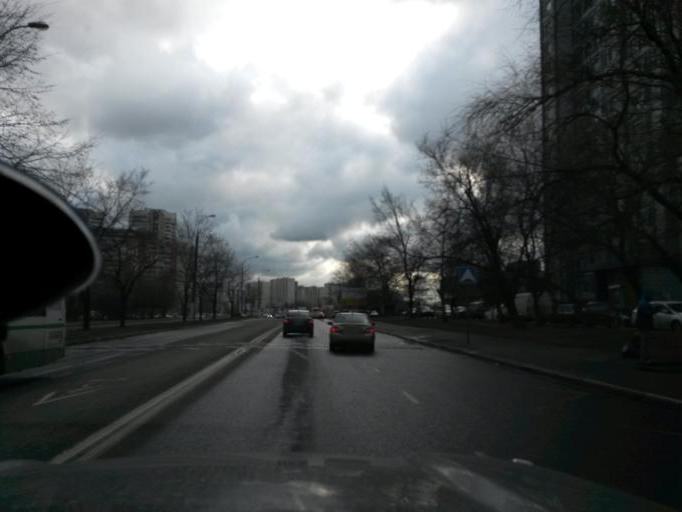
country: RU
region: Moscow
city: Brateyevo
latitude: 55.6304
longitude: 37.7476
